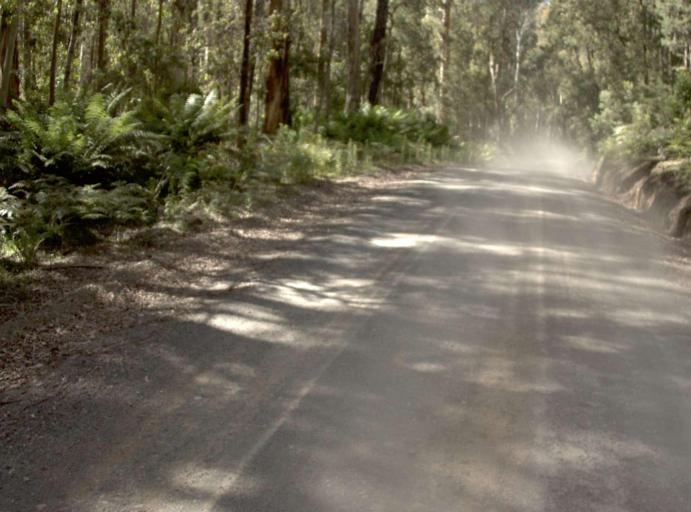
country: AU
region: New South Wales
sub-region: Bombala
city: Bombala
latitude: -37.2375
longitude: 148.7557
